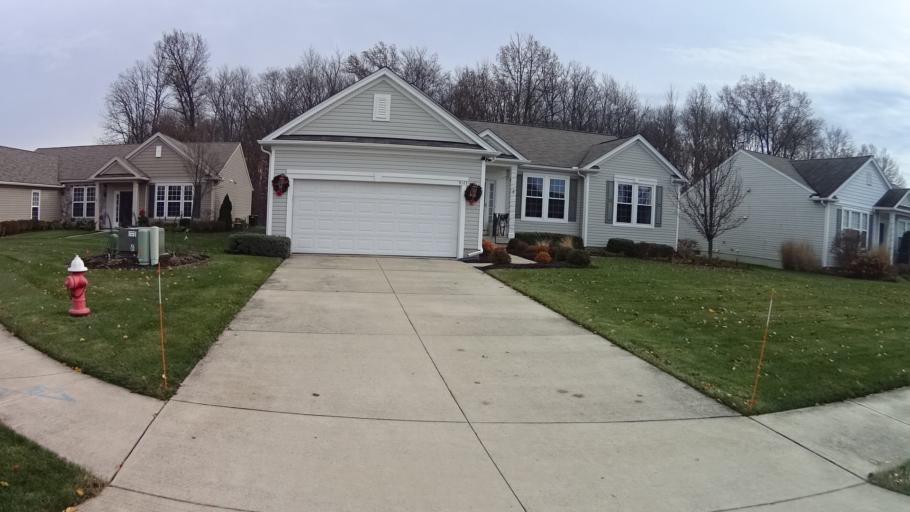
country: US
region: Ohio
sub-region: Lorain County
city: North Ridgeville
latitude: 41.3584
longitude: -82.0541
